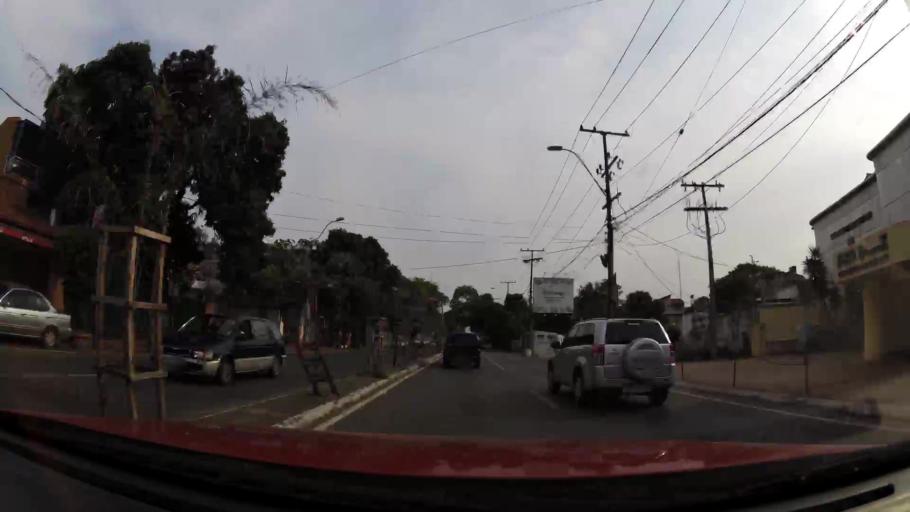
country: PY
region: Asuncion
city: Asuncion
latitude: -25.2972
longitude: -57.6121
